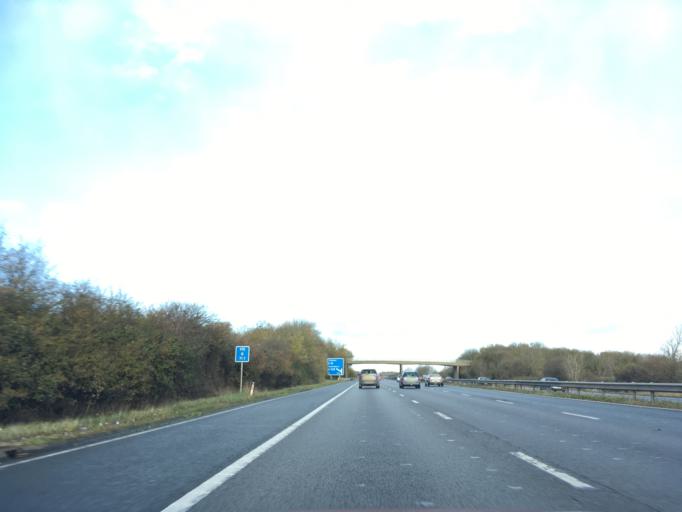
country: GB
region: England
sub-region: Gloucestershire
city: Tewkesbury
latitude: 51.9820
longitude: -2.1262
